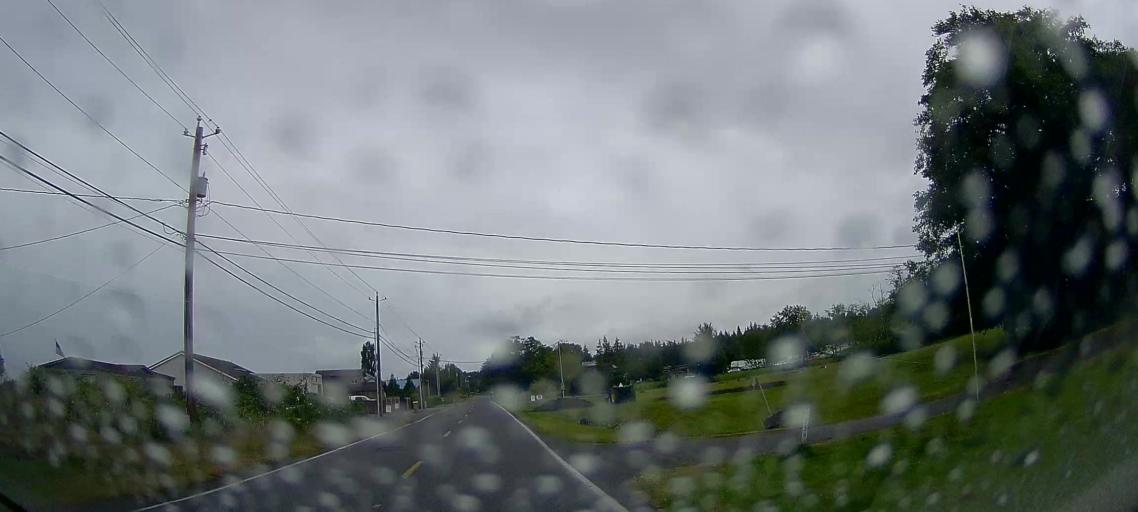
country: US
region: Washington
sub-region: Whatcom County
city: Birch Bay
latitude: 48.8067
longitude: -122.7089
